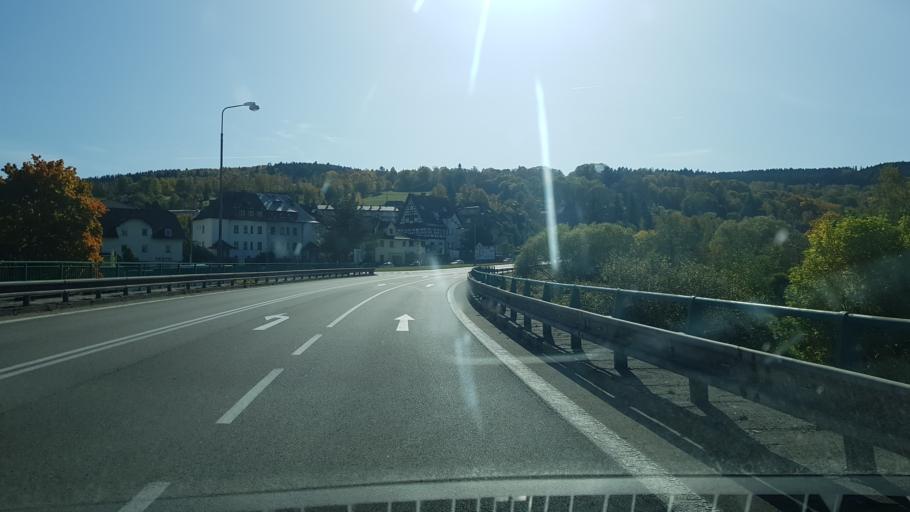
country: CZ
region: Jihocesky
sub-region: Okres Prachatice
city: Vimperk
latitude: 49.0567
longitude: 13.7858
